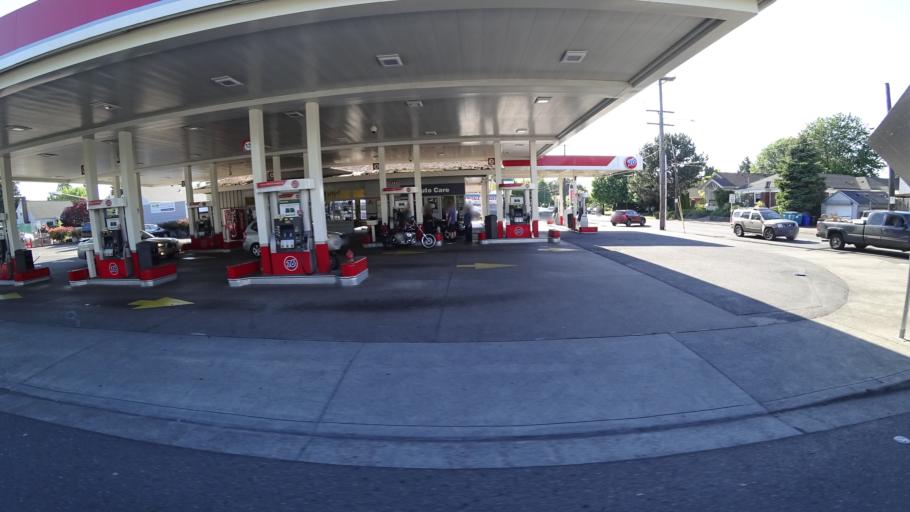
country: US
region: Oregon
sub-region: Multnomah County
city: Portland
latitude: 45.5625
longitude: -122.6824
